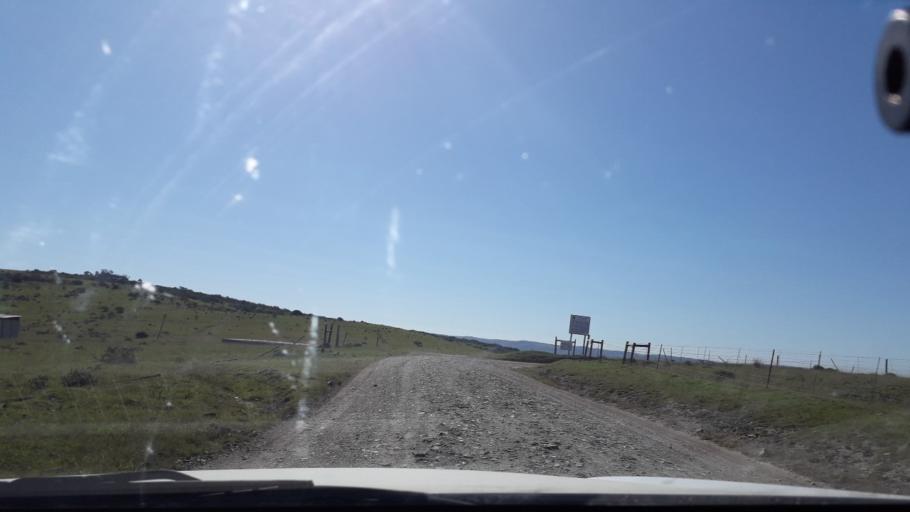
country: ZA
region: Eastern Cape
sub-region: Amathole District Municipality
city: Komga
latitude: -32.7928
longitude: 27.9516
